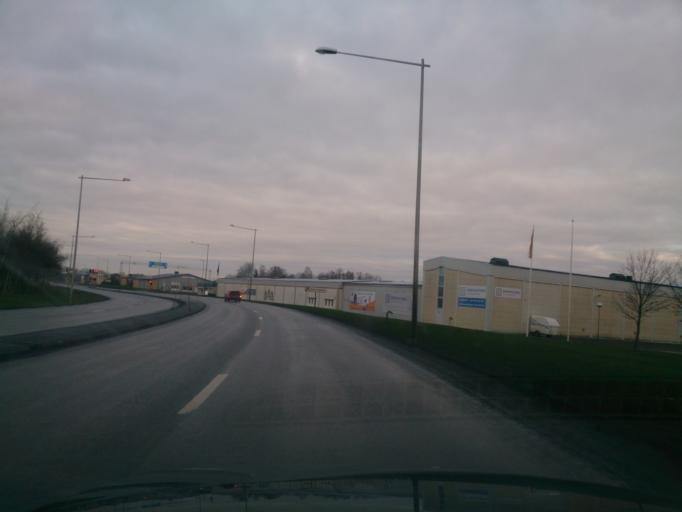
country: SE
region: OEstergoetland
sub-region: Linkopings Kommun
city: Linkoping
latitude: 58.4261
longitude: 15.6144
